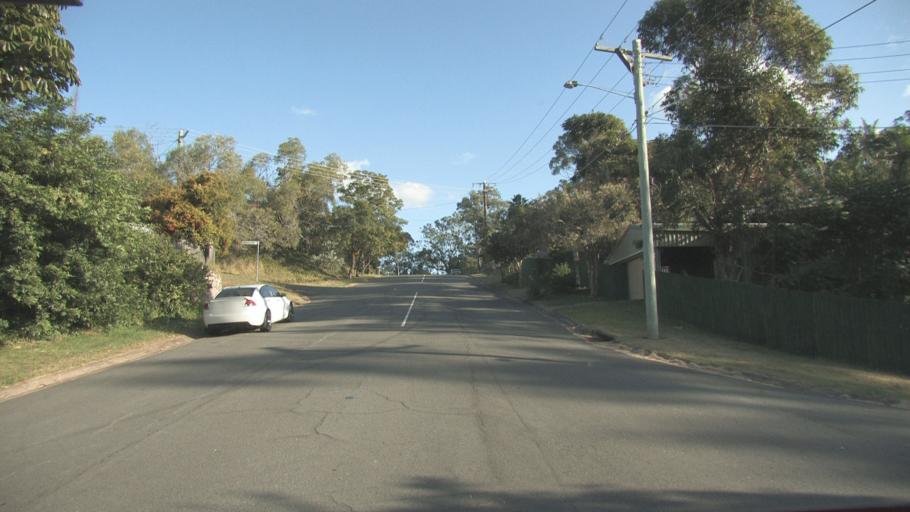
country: AU
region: Queensland
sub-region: Logan
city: Windaroo
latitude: -27.7250
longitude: 153.1906
